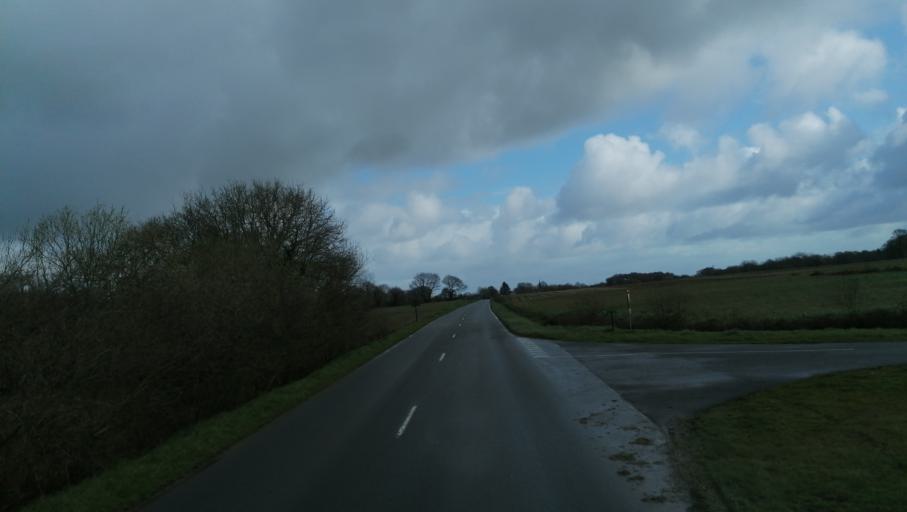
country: FR
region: Brittany
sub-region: Departement des Cotes-d'Armor
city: Lanrodec
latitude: 48.5238
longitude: -3.0228
